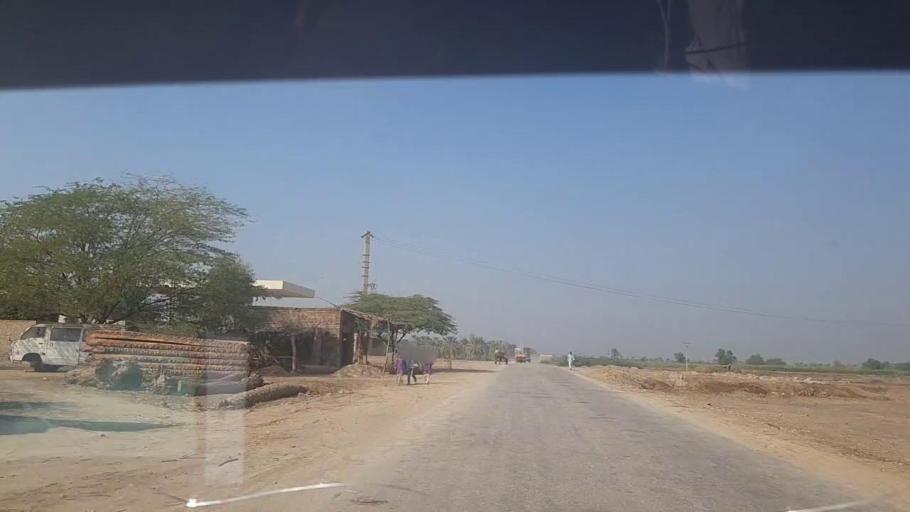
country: PK
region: Sindh
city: Kot Diji
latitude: 27.4153
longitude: 68.6648
